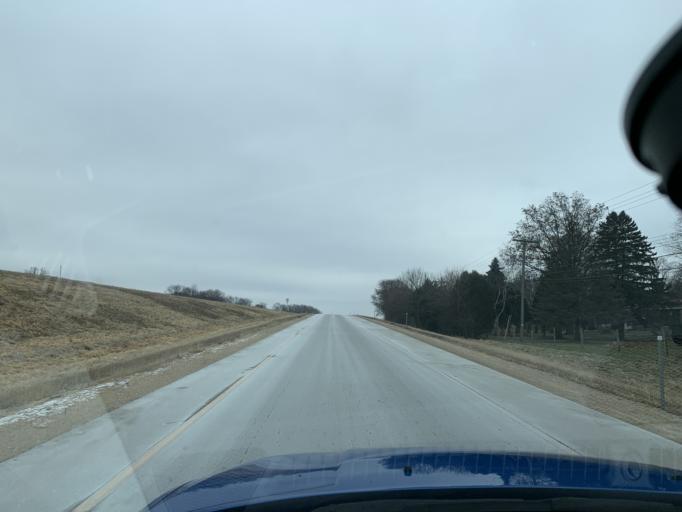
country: US
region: Wisconsin
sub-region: Dane County
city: Sun Prairie
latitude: 43.1970
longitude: -89.2098
